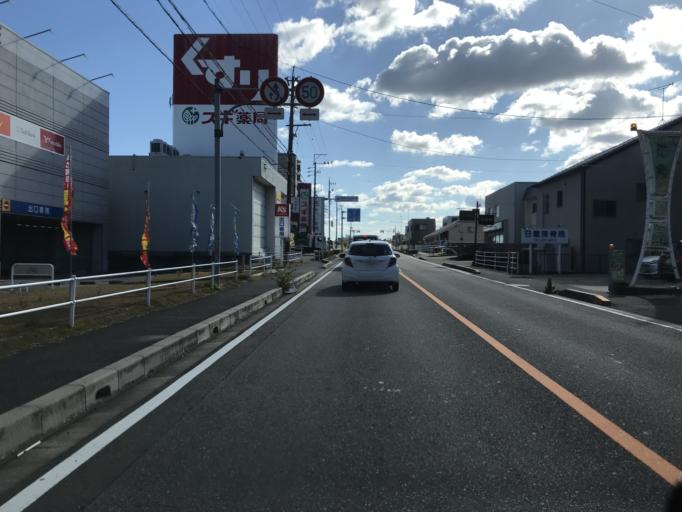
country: JP
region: Aichi
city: Nagoya-shi
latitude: 35.2070
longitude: 136.8565
